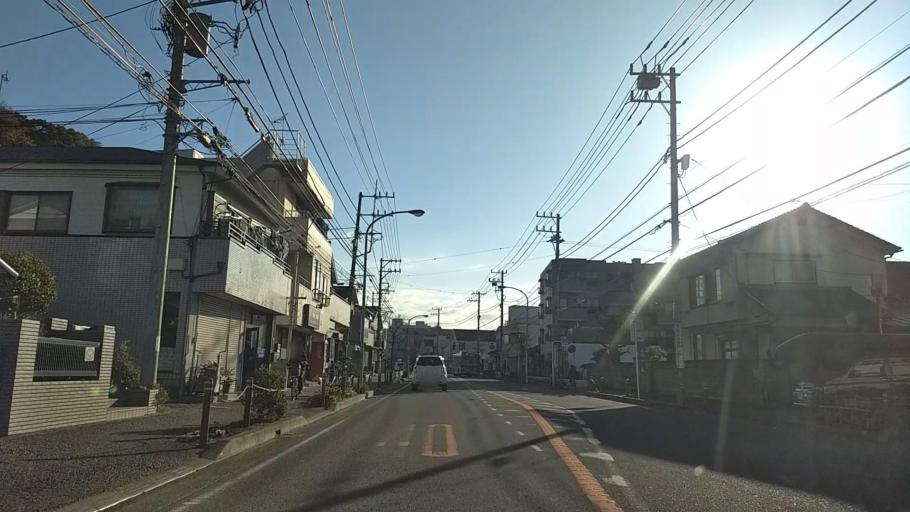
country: JP
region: Kanagawa
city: Fujisawa
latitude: 35.3471
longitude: 139.4699
